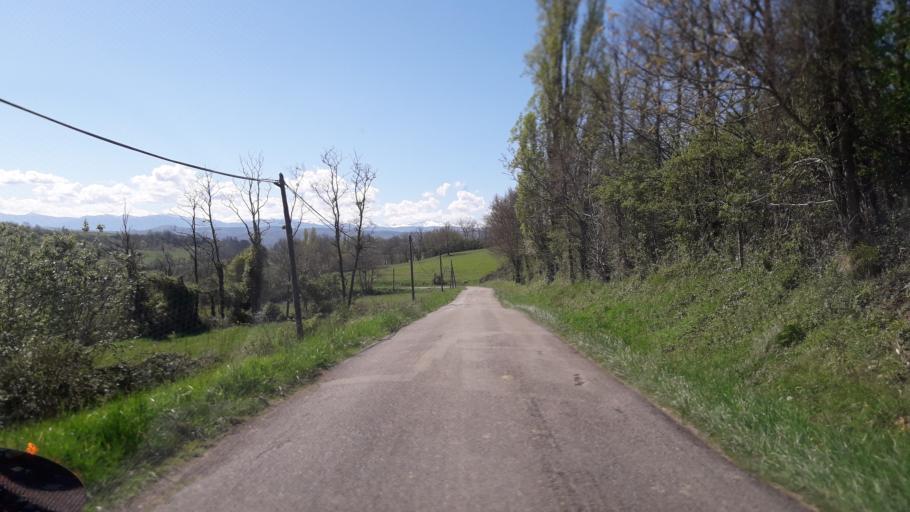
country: FR
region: Midi-Pyrenees
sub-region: Departement de la Haute-Garonne
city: Montesquieu-Volvestre
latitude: 43.1646
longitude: 1.3185
